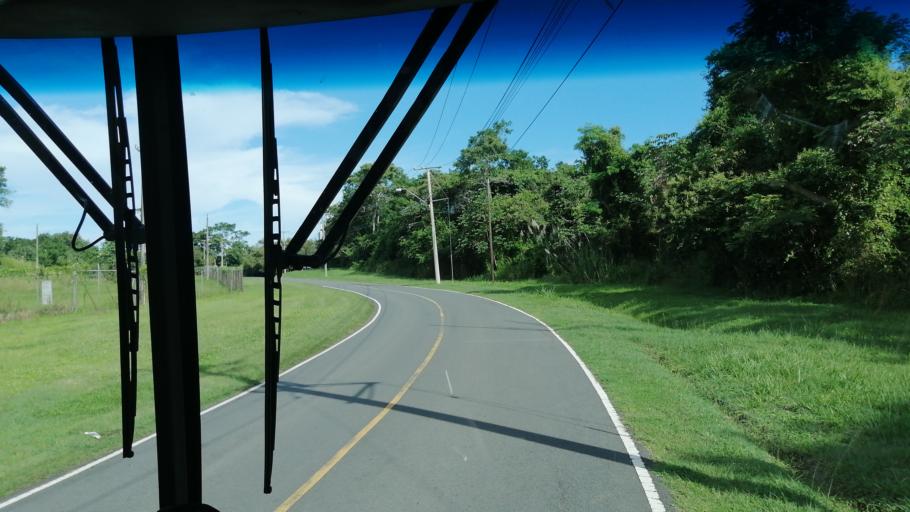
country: PA
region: Panama
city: Veracruz
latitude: 8.9010
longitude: -79.5856
